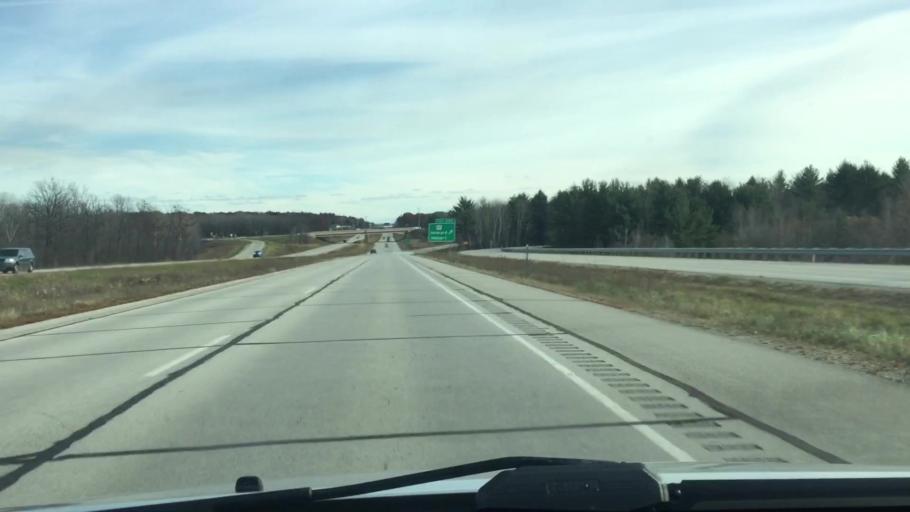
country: US
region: Wisconsin
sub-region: Brown County
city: Howard
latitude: 44.5631
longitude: -88.1370
